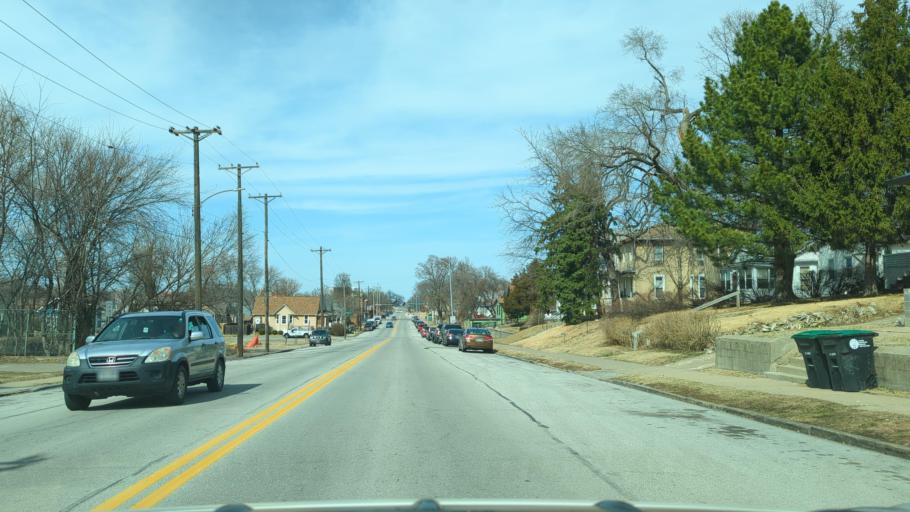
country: US
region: Nebraska
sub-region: Douglas County
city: Omaha
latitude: 41.2400
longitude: -95.9294
